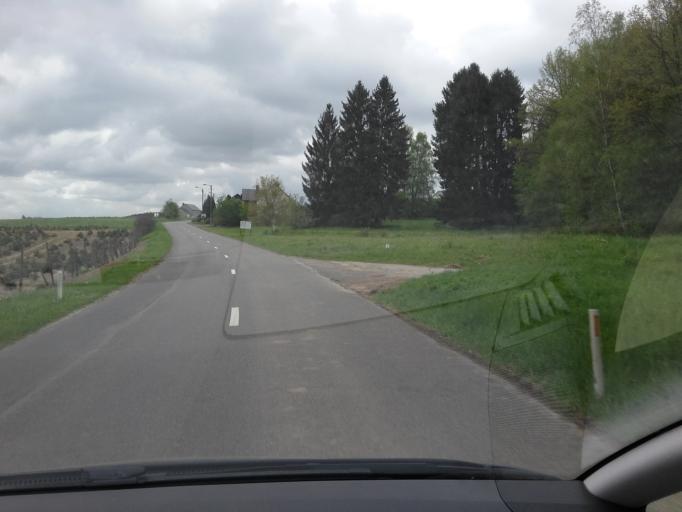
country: BE
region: Wallonia
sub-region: Province du Luxembourg
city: Bertrix
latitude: 49.8267
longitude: 5.3190
